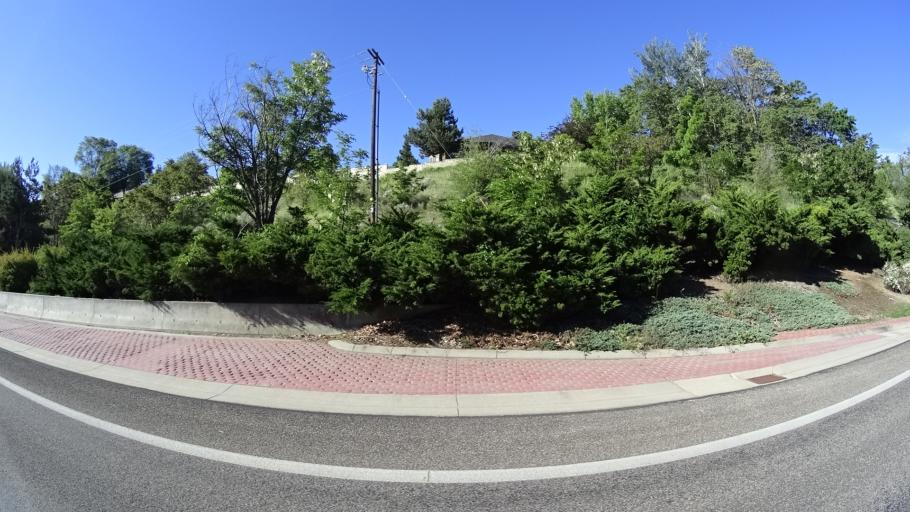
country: US
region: Idaho
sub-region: Ada County
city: Garden City
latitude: 43.6182
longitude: -116.2358
